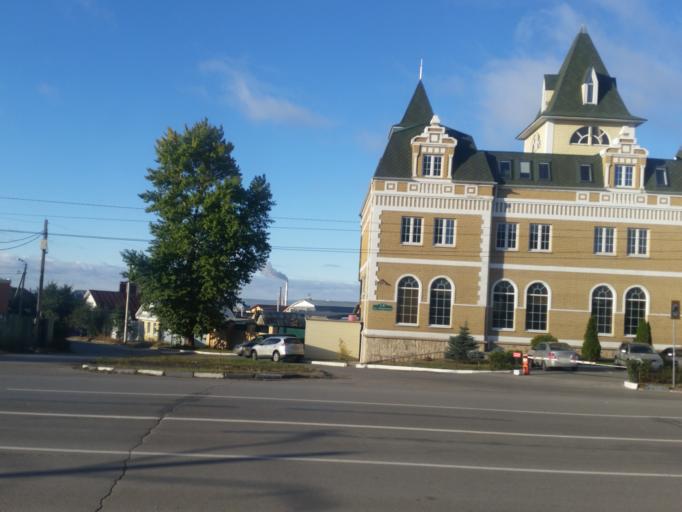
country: RU
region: Ulyanovsk
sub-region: Ulyanovskiy Rayon
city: Ulyanovsk
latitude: 54.3349
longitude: 48.3840
